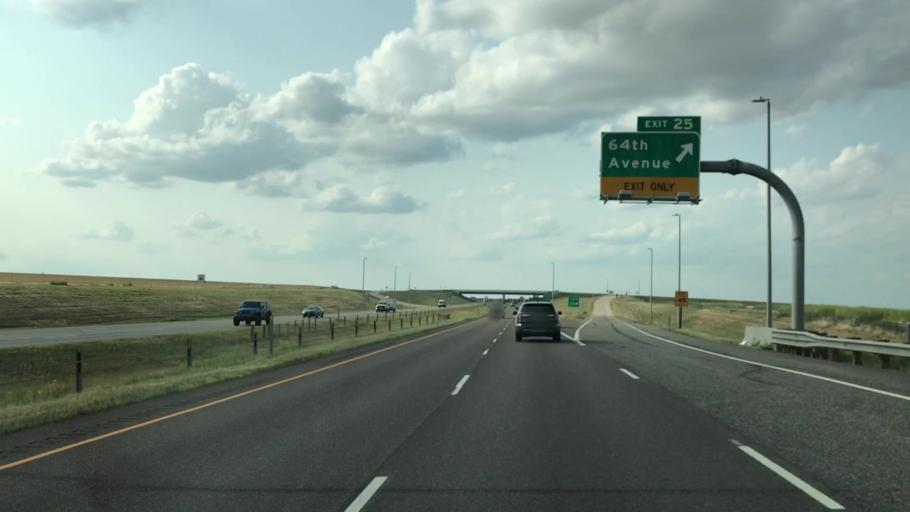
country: US
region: Colorado
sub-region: Adams County
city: Aurora
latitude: 39.8073
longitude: -104.7174
